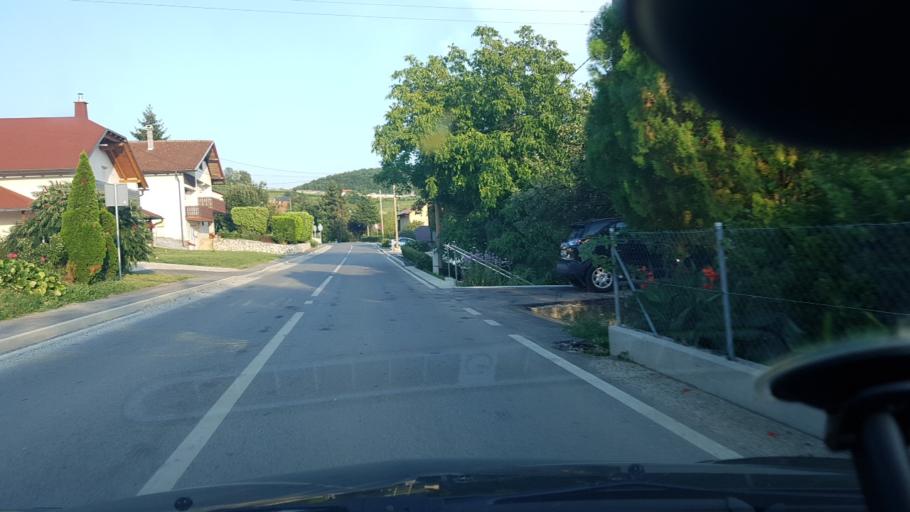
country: HR
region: Krapinsko-Zagorska
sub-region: Grad Krapina
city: Krapina
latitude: 46.1705
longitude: 15.8359
